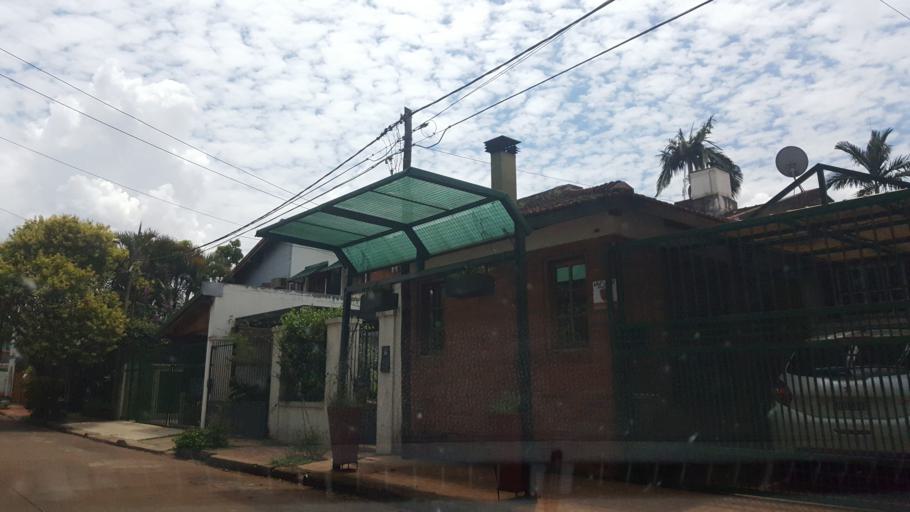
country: AR
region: Misiones
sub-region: Departamento de Capital
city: Posadas
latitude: -27.3808
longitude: -55.9075
